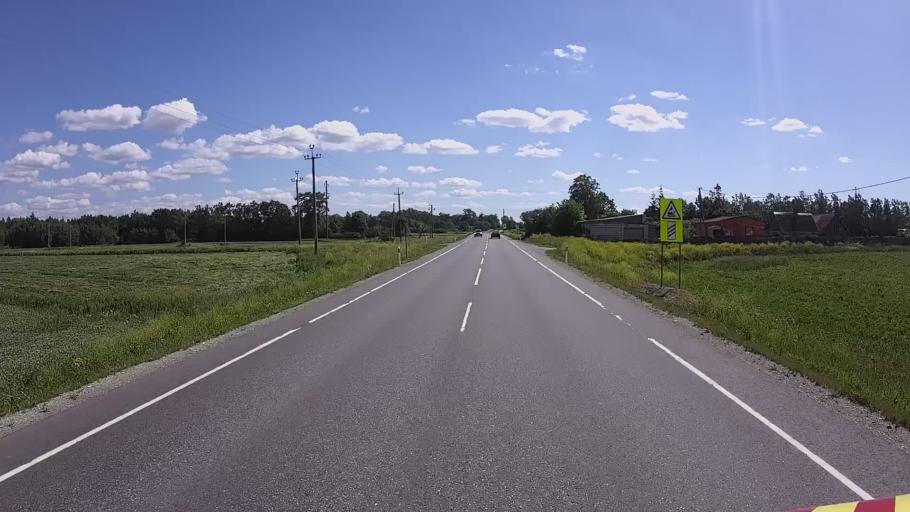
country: EE
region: Ida-Virumaa
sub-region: Johvi vald
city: Johvi
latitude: 59.3598
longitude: 27.3512
